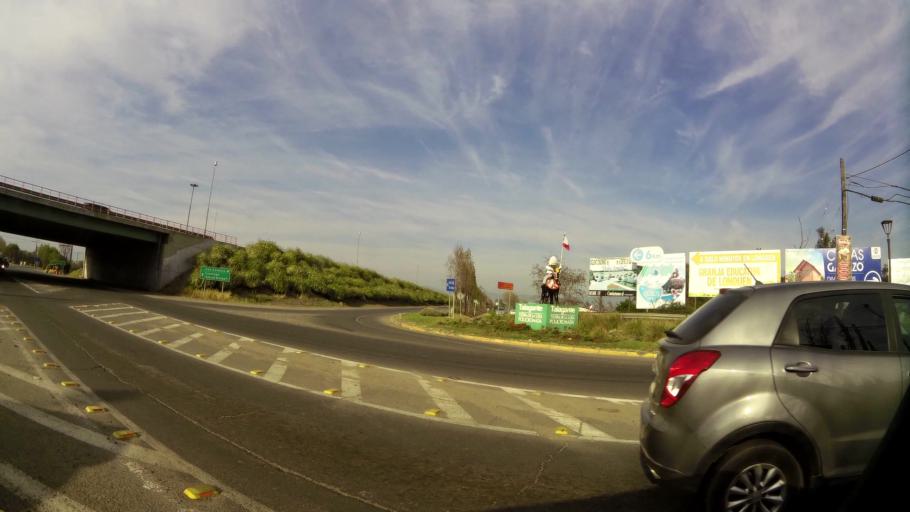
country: CL
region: Santiago Metropolitan
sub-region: Provincia de Talagante
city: Talagante
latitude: -33.6742
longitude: -70.9251
